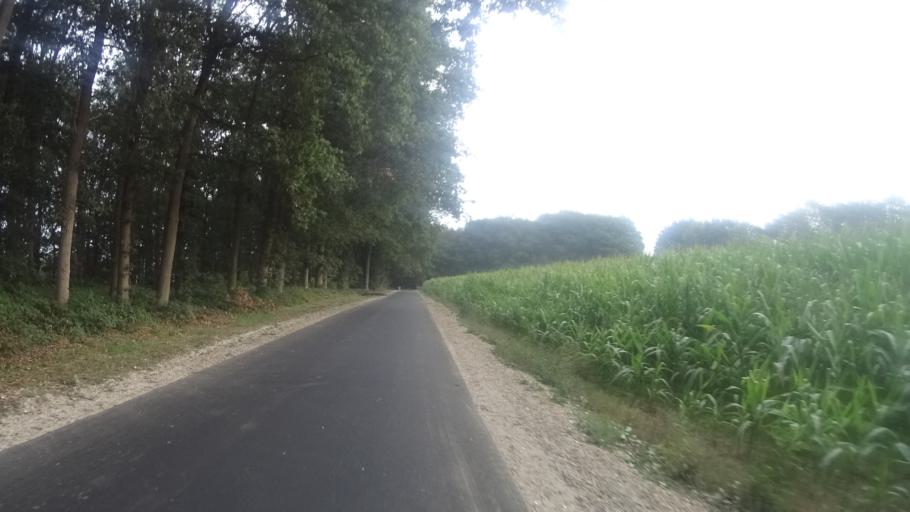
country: NL
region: Limburg
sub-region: Gemeente Venlo
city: Arcen
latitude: 51.4566
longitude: 6.1747
